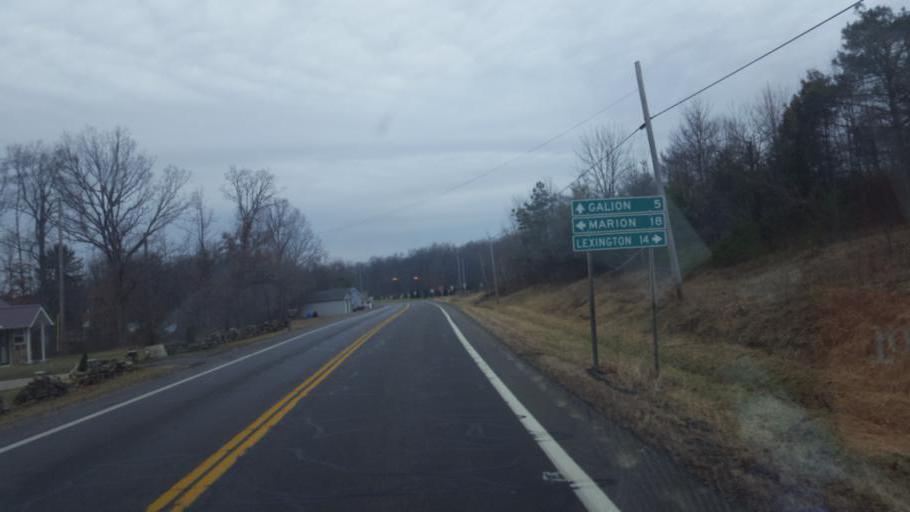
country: US
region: Ohio
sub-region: Crawford County
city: Galion
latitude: 40.6774
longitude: -82.8205
